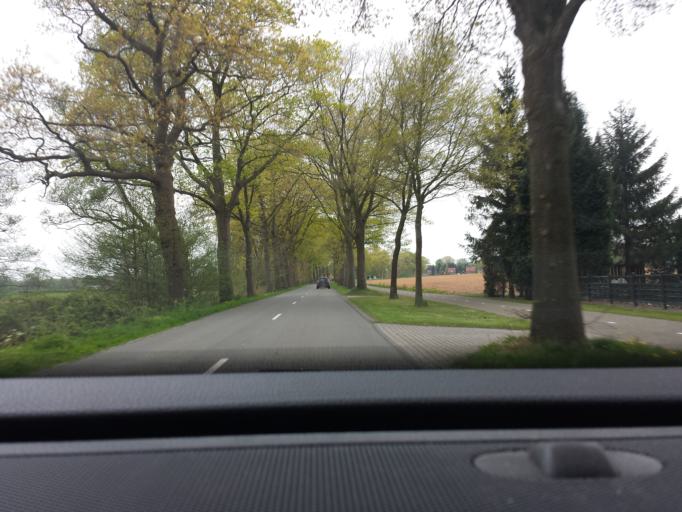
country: NL
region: Gelderland
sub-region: Gemeente Bronckhorst
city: Hengelo
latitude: 52.0577
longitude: 6.3307
